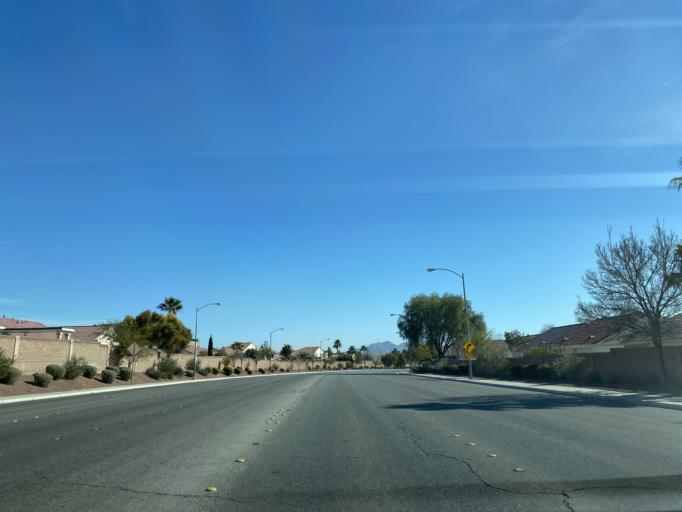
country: US
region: Nevada
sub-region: Clark County
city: North Las Vegas
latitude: 36.2818
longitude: -115.1466
